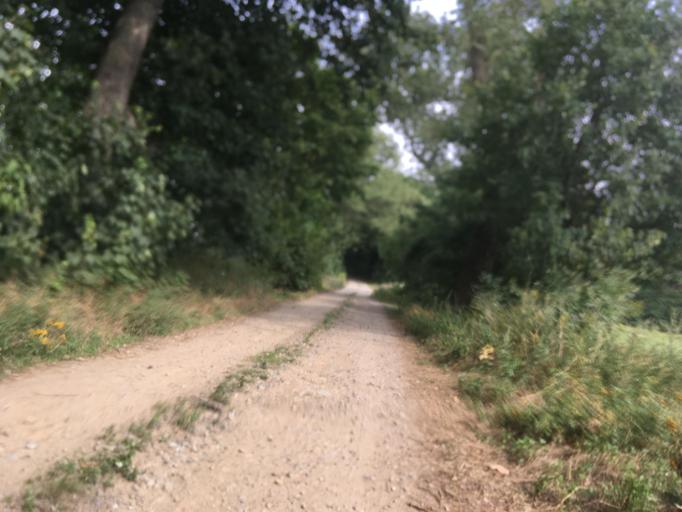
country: DE
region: Brandenburg
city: Rudnitz
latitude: 52.6890
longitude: 13.6377
